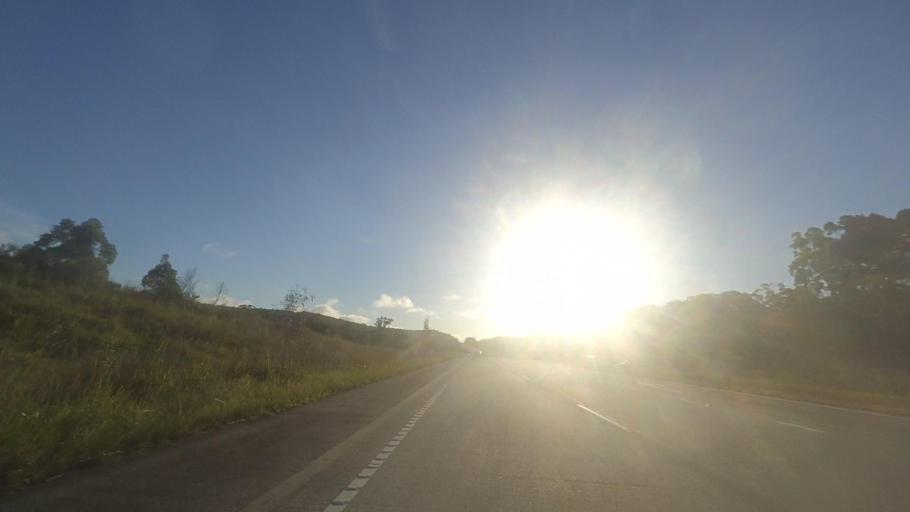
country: AU
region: New South Wales
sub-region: Great Lakes
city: Bulahdelah
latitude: -32.5267
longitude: 152.1929
